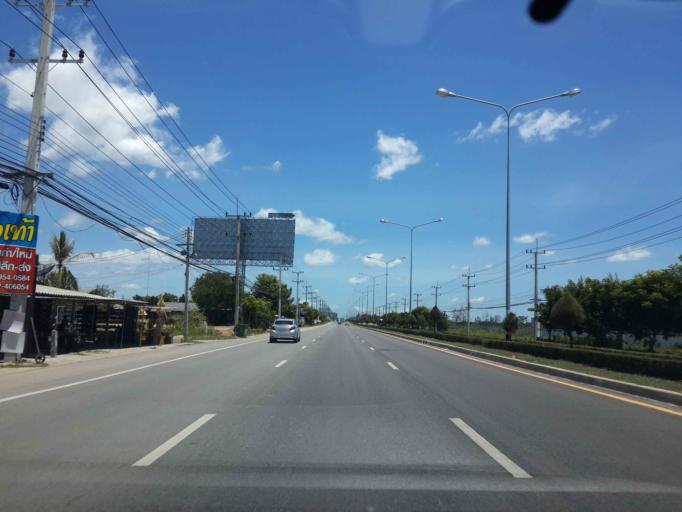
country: TH
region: Phetchaburi
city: Cha-am
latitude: 12.6890
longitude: 99.9528
